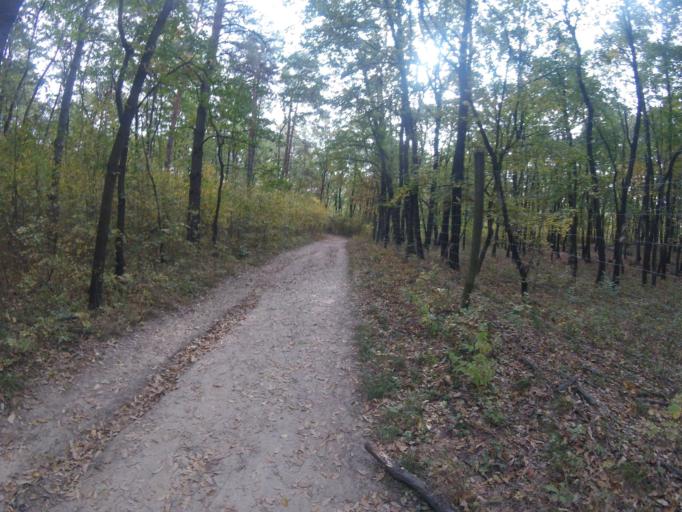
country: HU
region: Fejer
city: Bodajk
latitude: 47.3101
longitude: 18.2248
